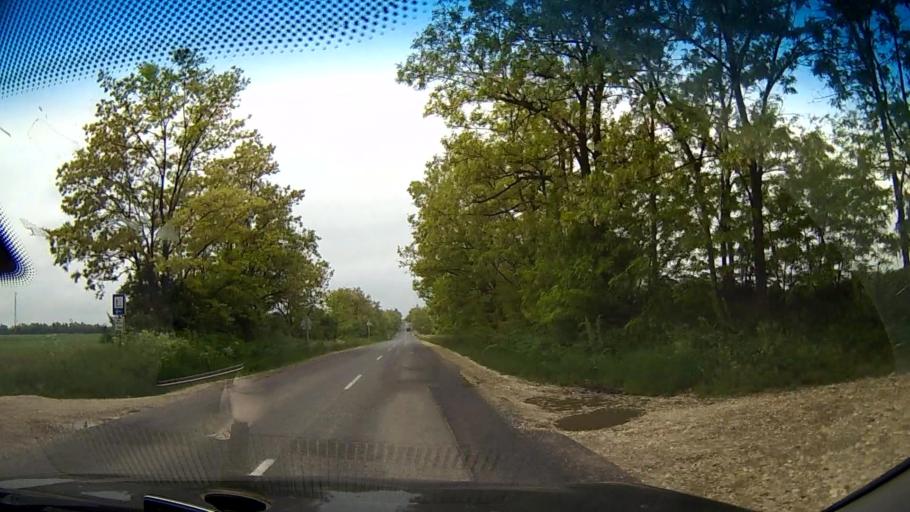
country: HU
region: Fejer
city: Many
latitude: 47.5190
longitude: 18.6497
